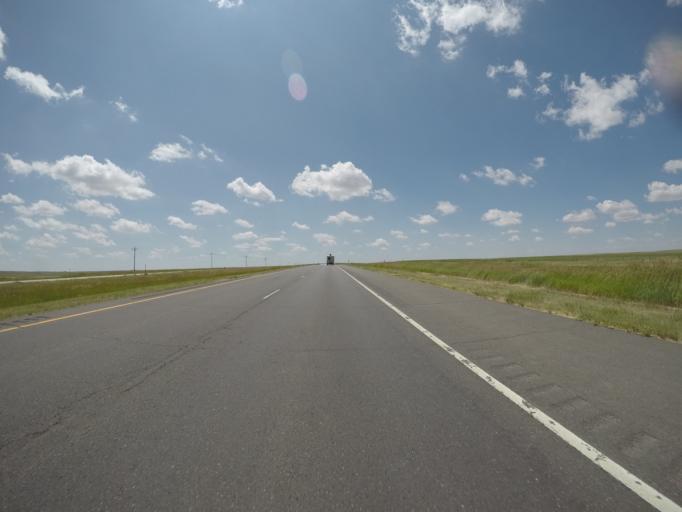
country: US
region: Colorado
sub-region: Lincoln County
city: Hugo
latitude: 39.2868
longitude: -102.9173
